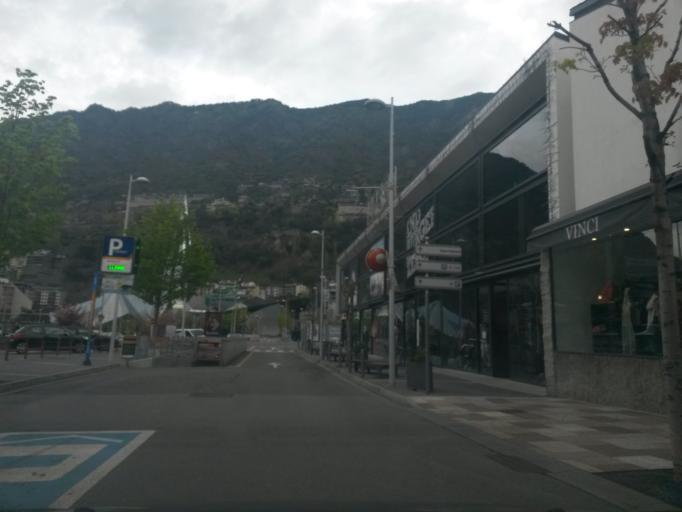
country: AD
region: Escaldes-Engordany
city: les Escaldes
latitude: 42.5091
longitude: 1.5379
